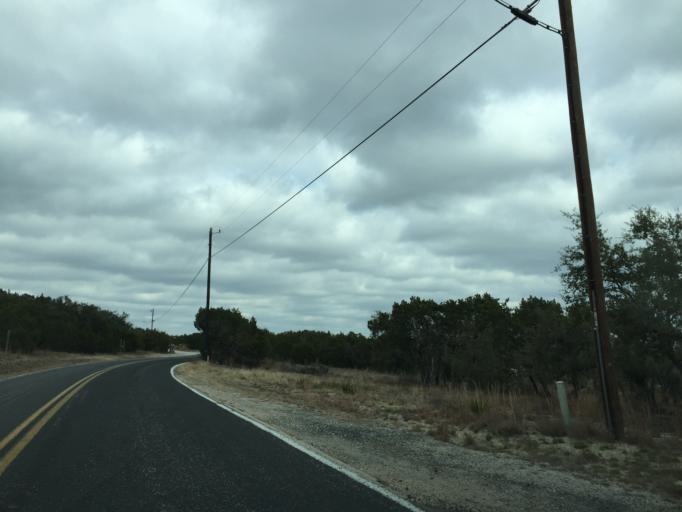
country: US
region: Texas
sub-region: Travis County
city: Briarcliff
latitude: 30.3736
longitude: -98.0916
